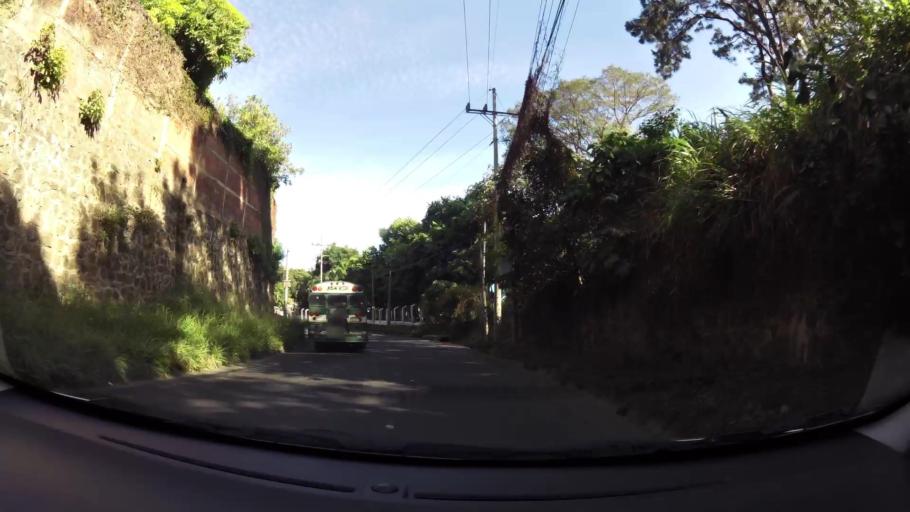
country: SV
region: Santa Ana
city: Santa Ana
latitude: 13.9807
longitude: -89.5824
